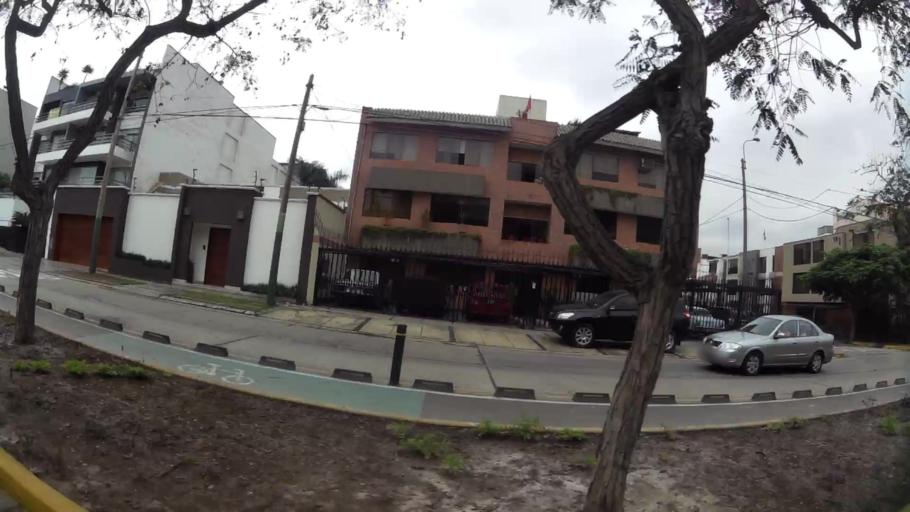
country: PE
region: Lima
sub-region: Lima
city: San Luis
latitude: -12.1088
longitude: -76.9799
